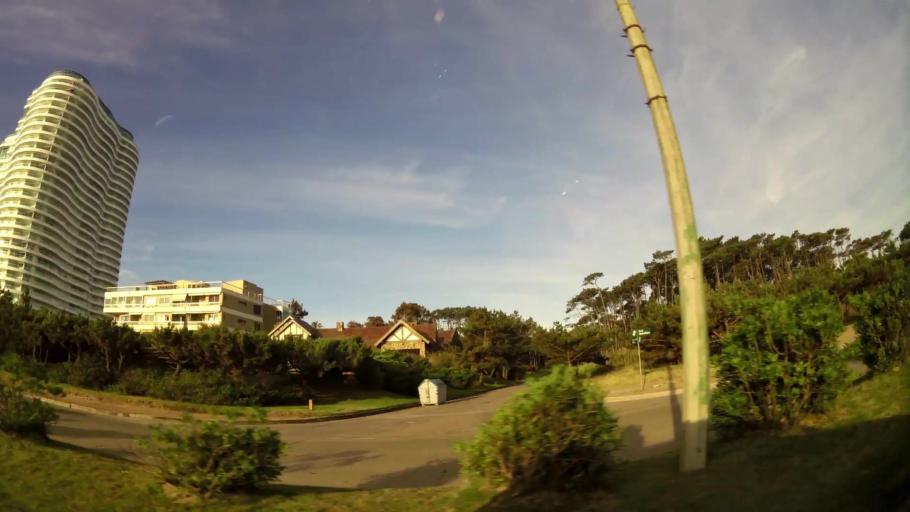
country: UY
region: Maldonado
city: Maldonado
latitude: -34.9290
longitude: -54.9603
